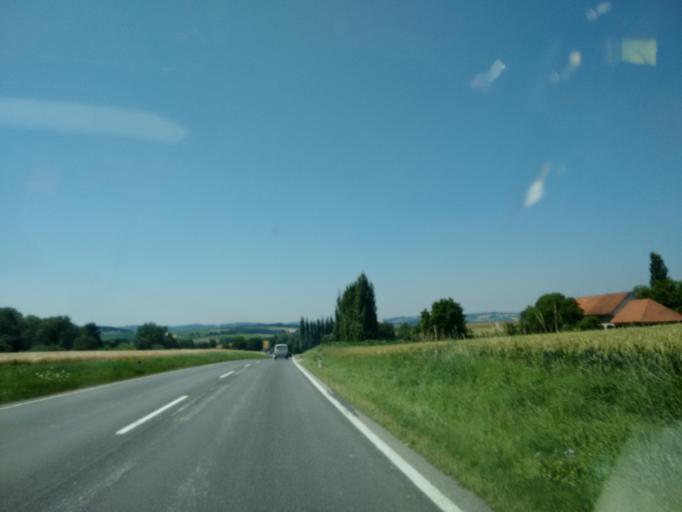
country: AT
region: Upper Austria
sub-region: Wels-Land
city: Buchkirchen
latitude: 48.1954
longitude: 13.9969
